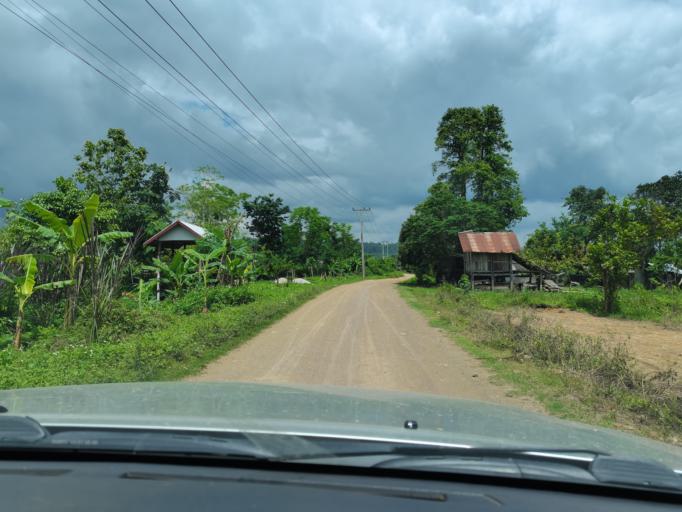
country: LA
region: Loungnamtha
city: Muang Long
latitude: 20.6819
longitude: 101.0516
